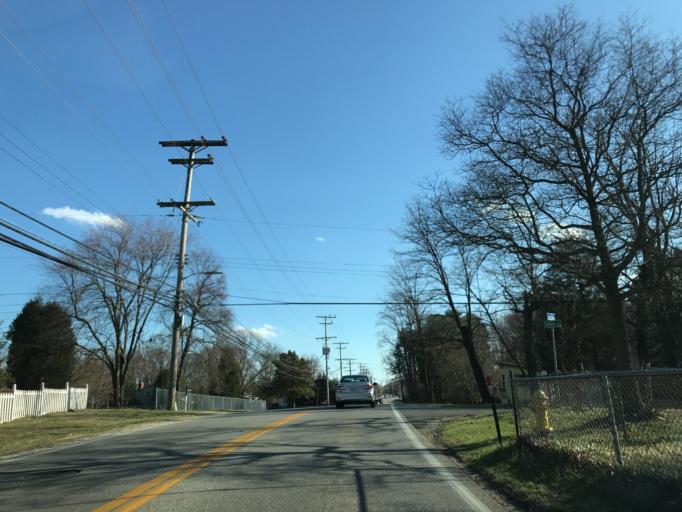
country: US
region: Maryland
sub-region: Anne Arundel County
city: Green Haven
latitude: 39.1351
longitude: -76.5636
